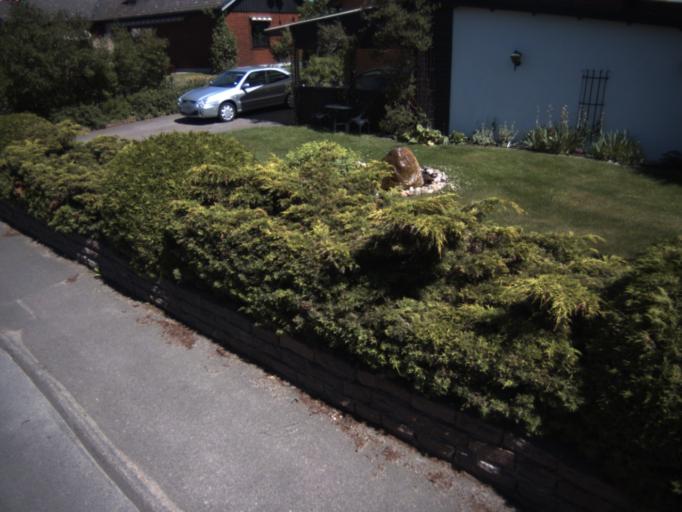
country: SE
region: Skane
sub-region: Helsingborg
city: Morarp
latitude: 56.0530
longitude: 12.8834
